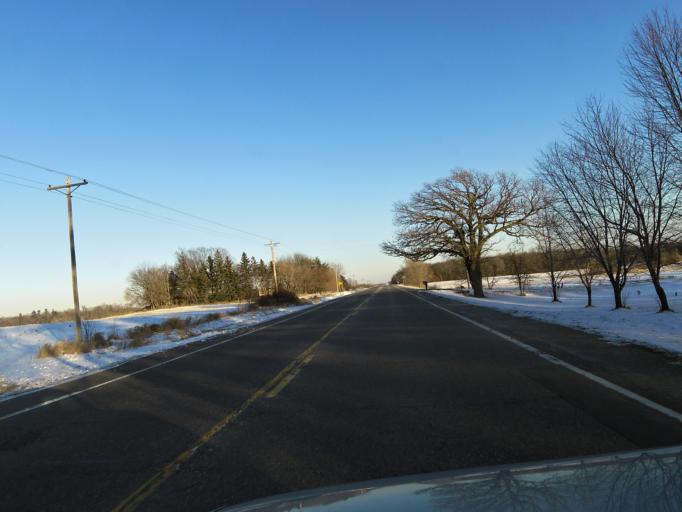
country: US
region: Minnesota
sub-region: Scott County
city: Elko New Market
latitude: 44.5439
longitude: -93.2585
